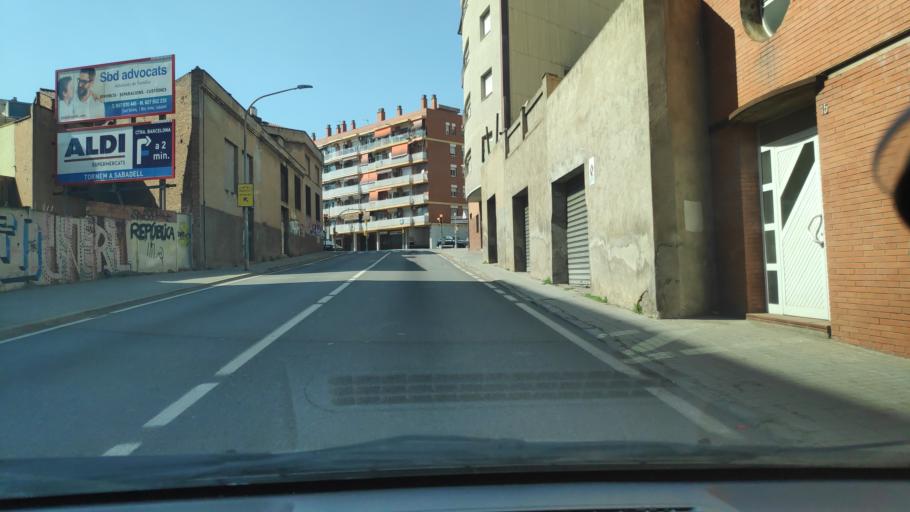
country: ES
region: Catalonia
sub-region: Provincia de Barcelona
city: Sabadell
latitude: 41.5348
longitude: 2.1167
